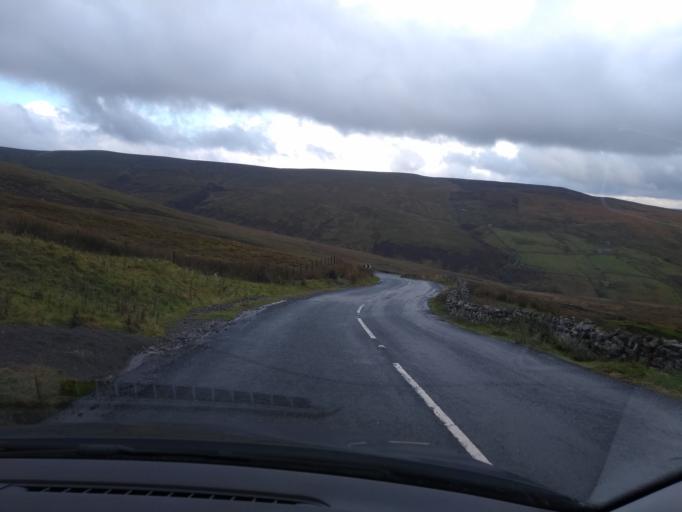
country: GB
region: England
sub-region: Cumbria
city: Kirkby Stephen
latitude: 54.3698
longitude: -2.1873
